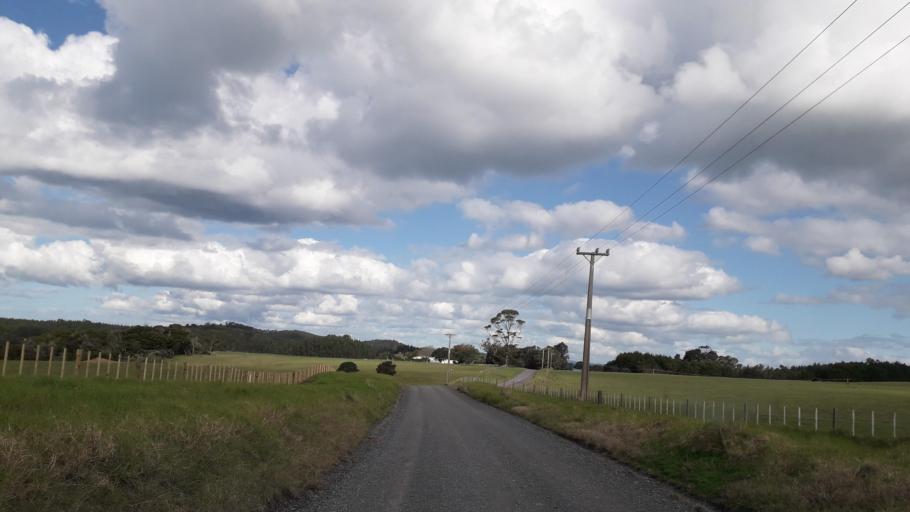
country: NZ
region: Northland
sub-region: Far North District
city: Kerikeri
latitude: -35.1486
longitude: 174.0387
